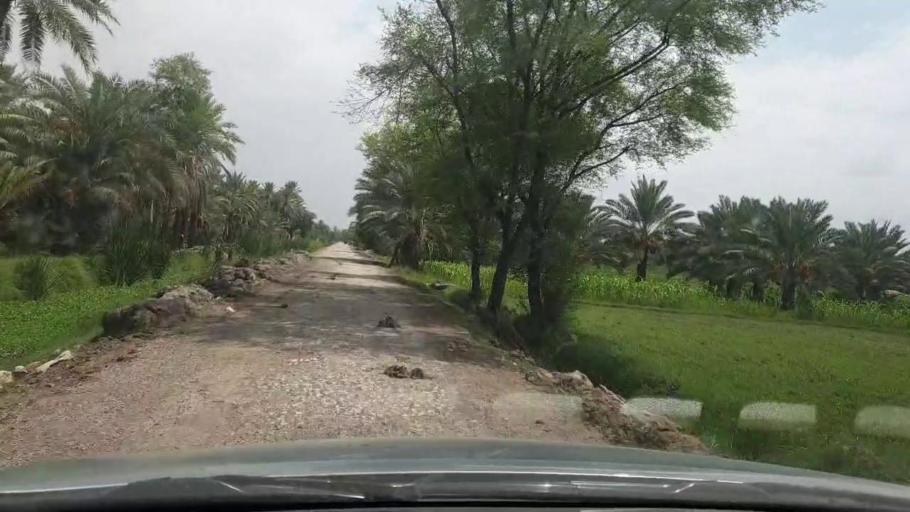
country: PK
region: Sindh
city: Kot Diji
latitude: 27.4137
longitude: 68.7599
